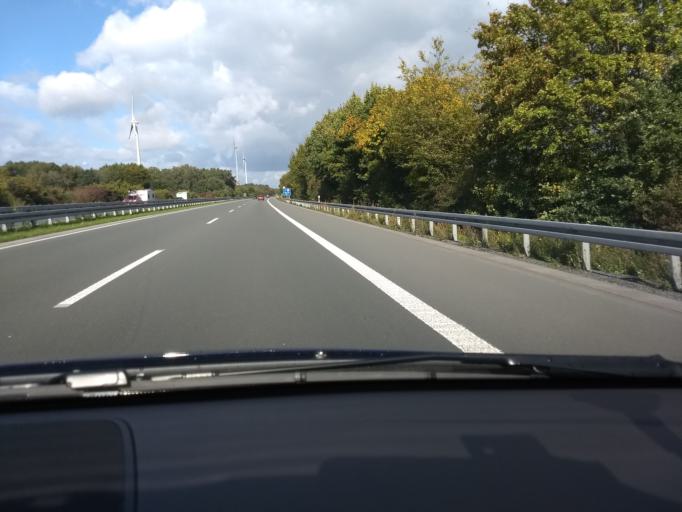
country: DE
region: North Rhine-Westphalia
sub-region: Regierungsbezirk Munster
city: Heiden
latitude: 51.7733
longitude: 6.9660
